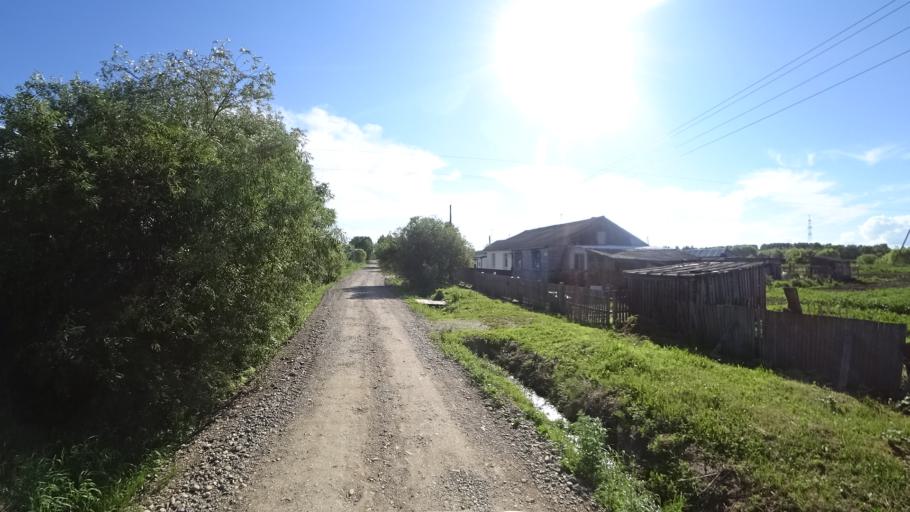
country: RU
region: Khabarovsk Krai
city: Khor
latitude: 47.8953
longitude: 134.9948
